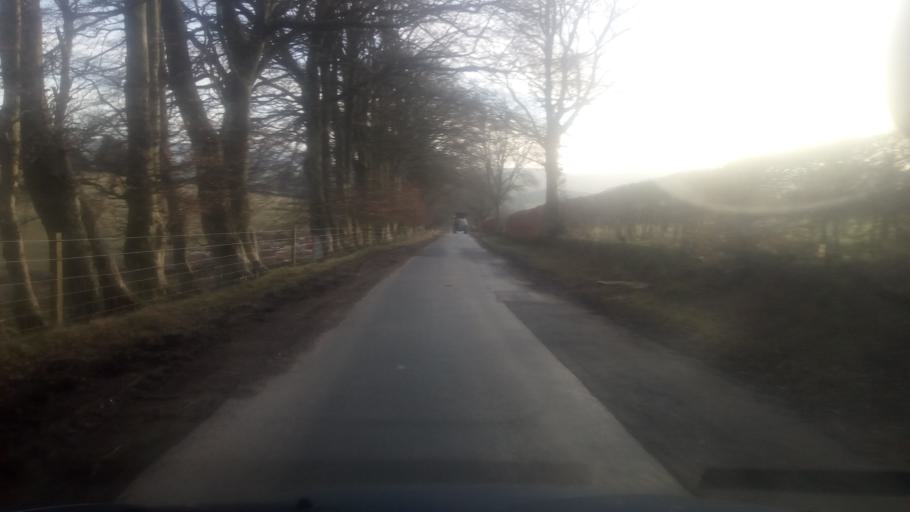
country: GB
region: Scotland
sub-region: The Scottish Borders
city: Jedburgh
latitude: 55.3938
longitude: -2.5937
